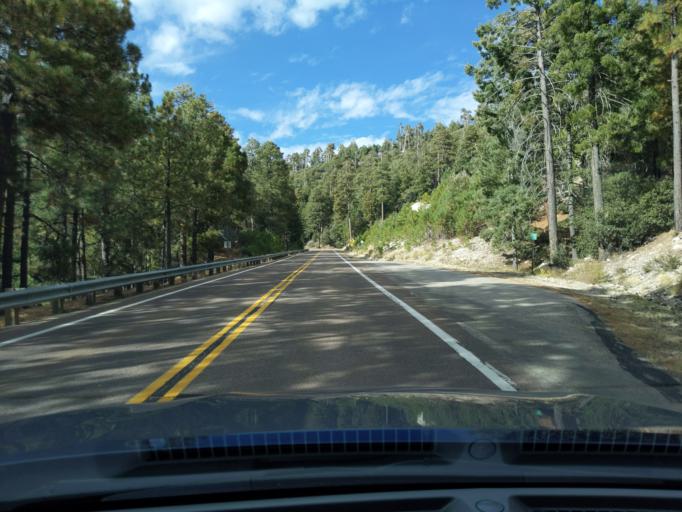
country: US
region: Arizona
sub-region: Pima County
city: Tanque Verde
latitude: 32.4074
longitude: -110.7040
